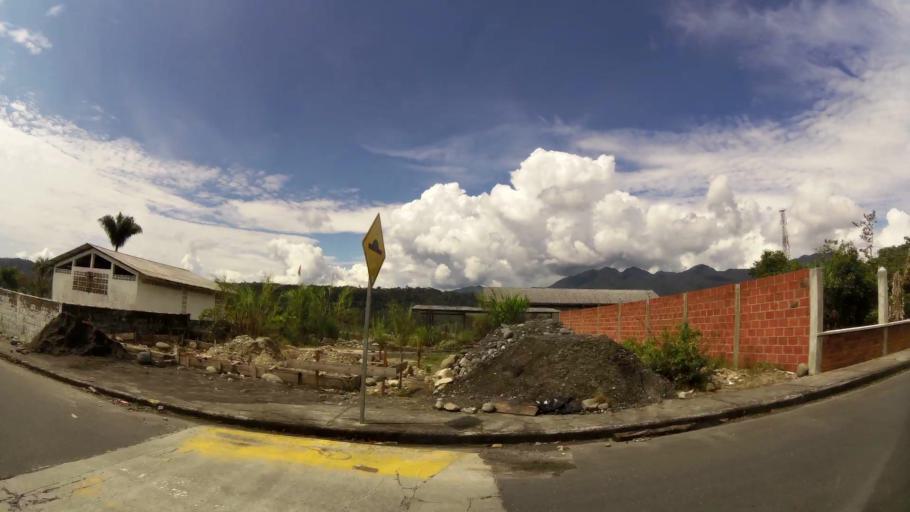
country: EC
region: Pastaza
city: Puyo
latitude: -1.4628
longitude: -78.1103
